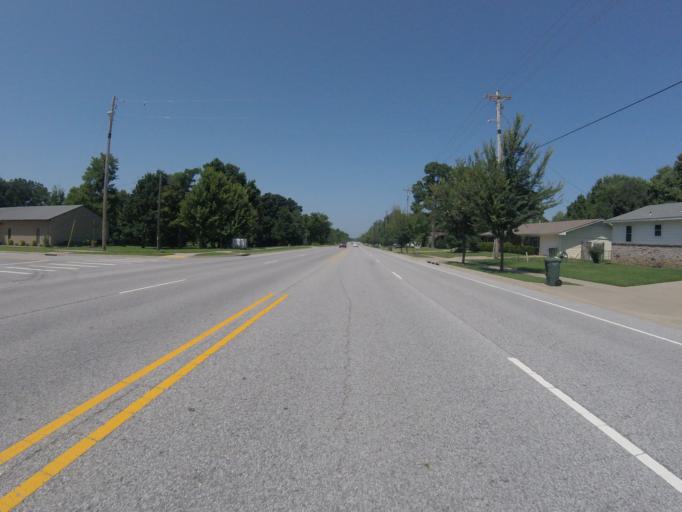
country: US
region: Arkansas
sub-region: Washington County
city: Fayetteville
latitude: 36.0927
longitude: -94.1979
